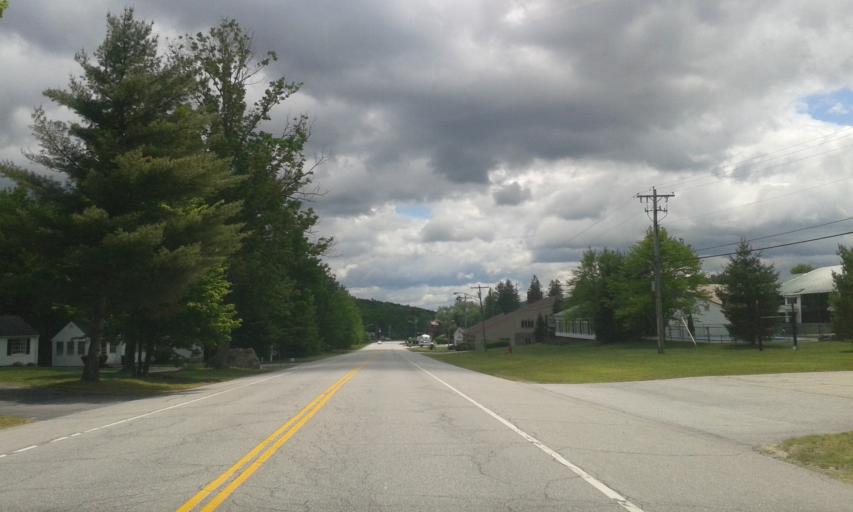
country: US
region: New Hampshire
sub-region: Grafton County
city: Woodstock
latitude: 44.0788
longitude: -71.6848
